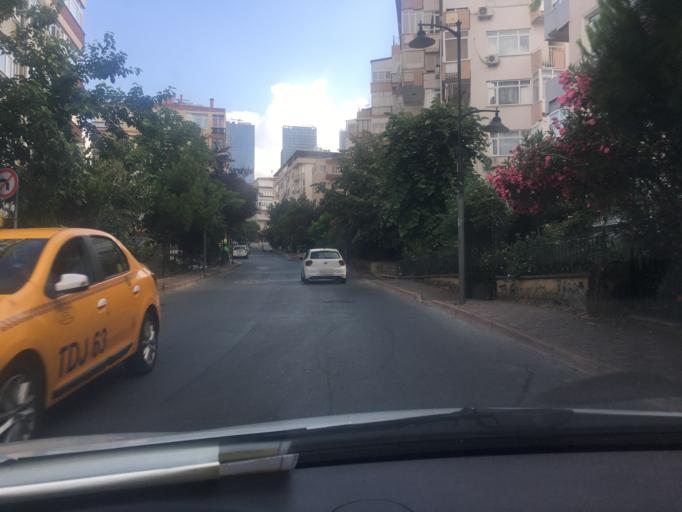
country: TR
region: Istanbul
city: Sisli
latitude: 41.0588
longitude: 28.9988
